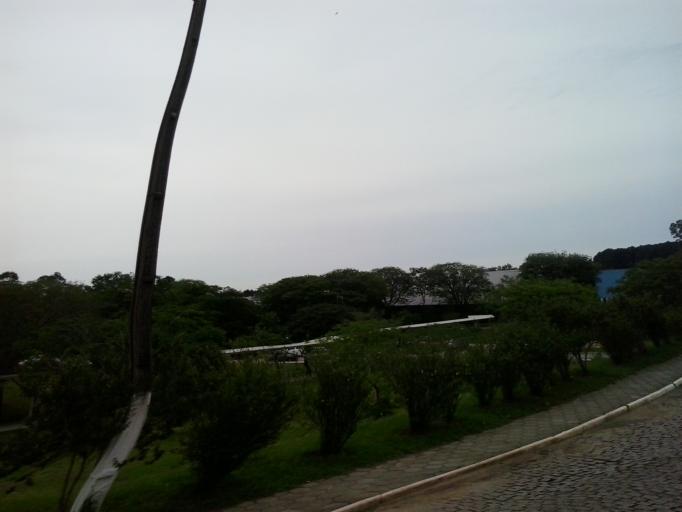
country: BR
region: Rio Grande do Sul
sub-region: Santa Maria
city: Santa Maria
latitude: -29.7160
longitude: -53.7157
